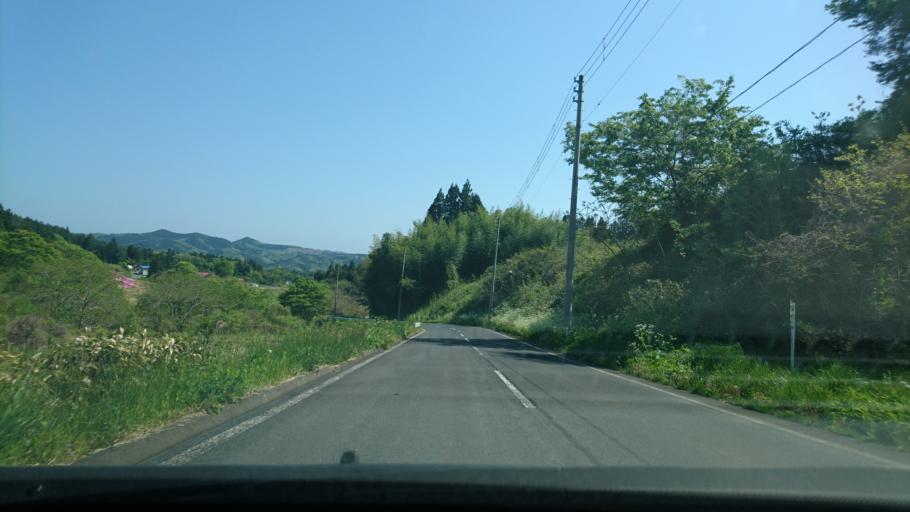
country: JP
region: Iwate
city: Ichinoseki
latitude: 38.9213
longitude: 141.2772
